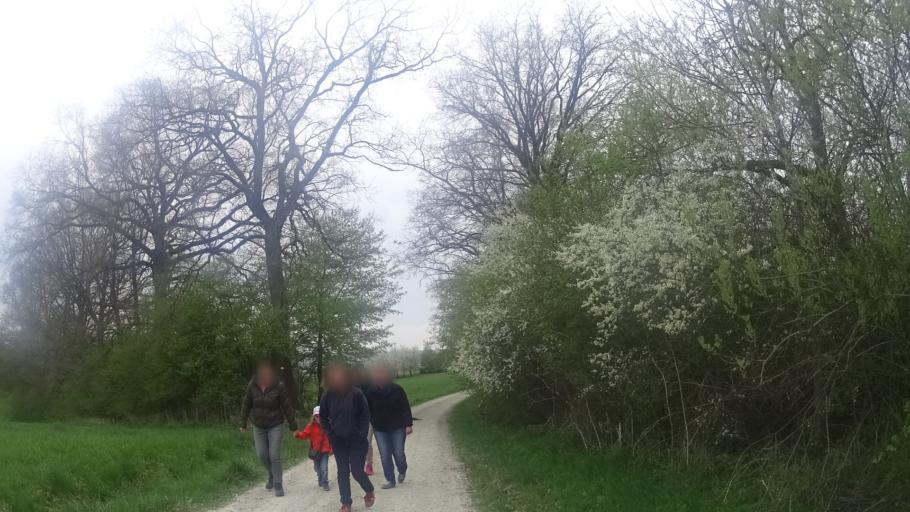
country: DE
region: Bavaria
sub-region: Upper Franconia
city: Kleinsendelbach
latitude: 49.5981
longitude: 11.1907
